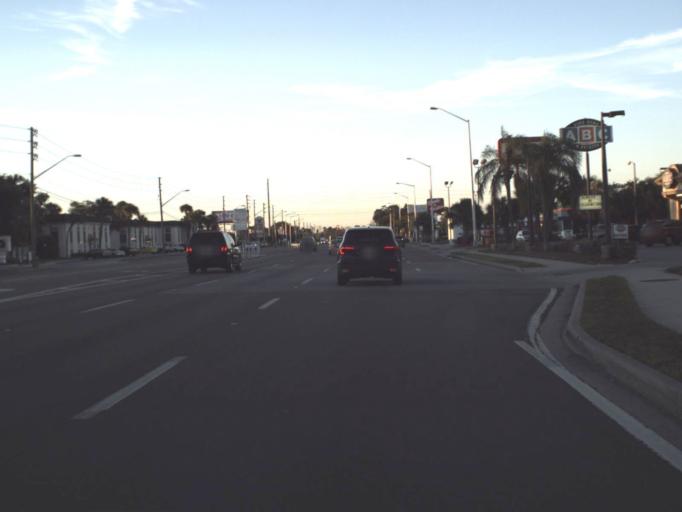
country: US
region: Florida
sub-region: Seminole County
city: Goldenrod
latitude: 28.6004
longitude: -81.3072
